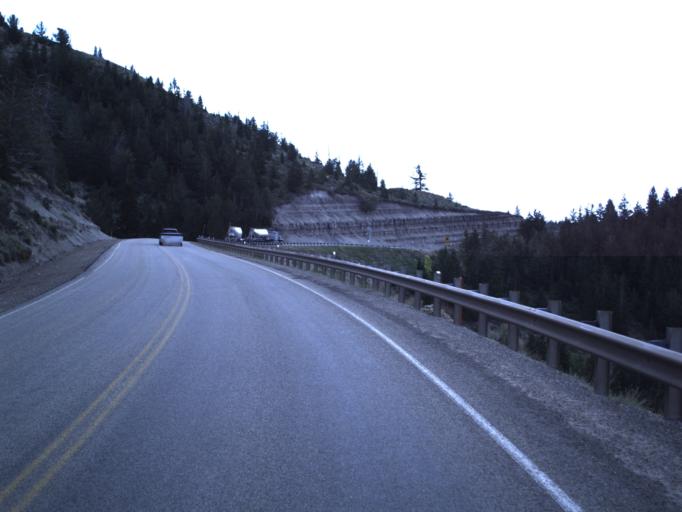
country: US
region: Utah
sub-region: Carbon County
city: Helper
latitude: 39.8878
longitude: -110.7496
